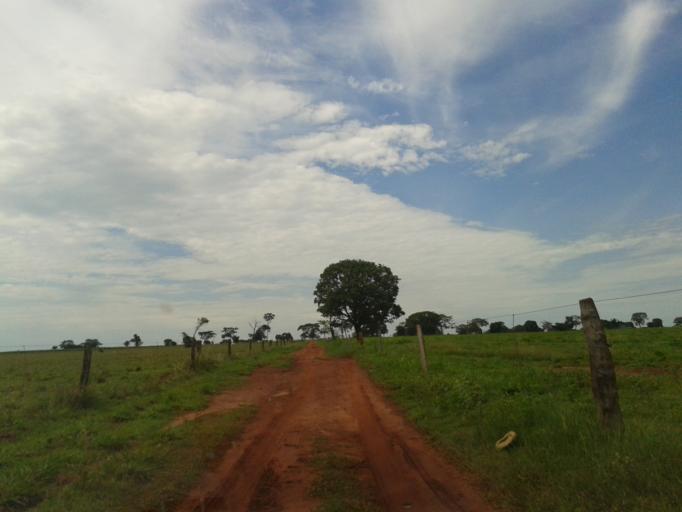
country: BR
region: Minas Gerais
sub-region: Santa Vitoria
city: Santa Vitoria
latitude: -19.1532
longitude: -50.6021
